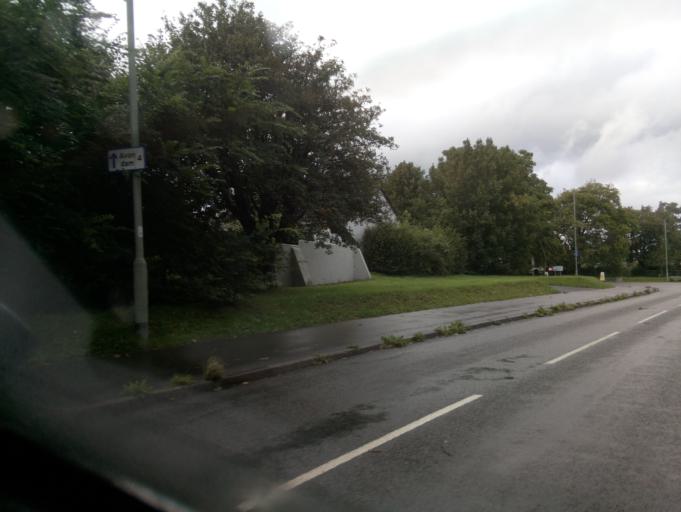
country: GB
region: England
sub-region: Devon
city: South Brent
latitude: 50.4239
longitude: -3.8300
